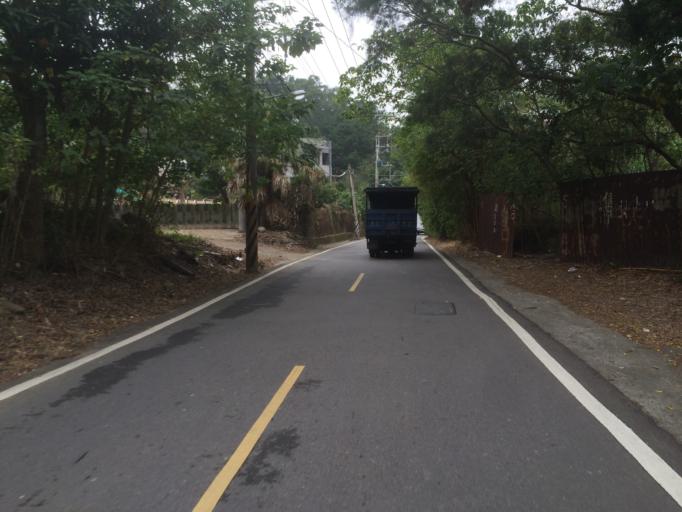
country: TW
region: Taiwan
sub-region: Taichung City
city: Taichung
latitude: 24.1616
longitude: 120.7454
